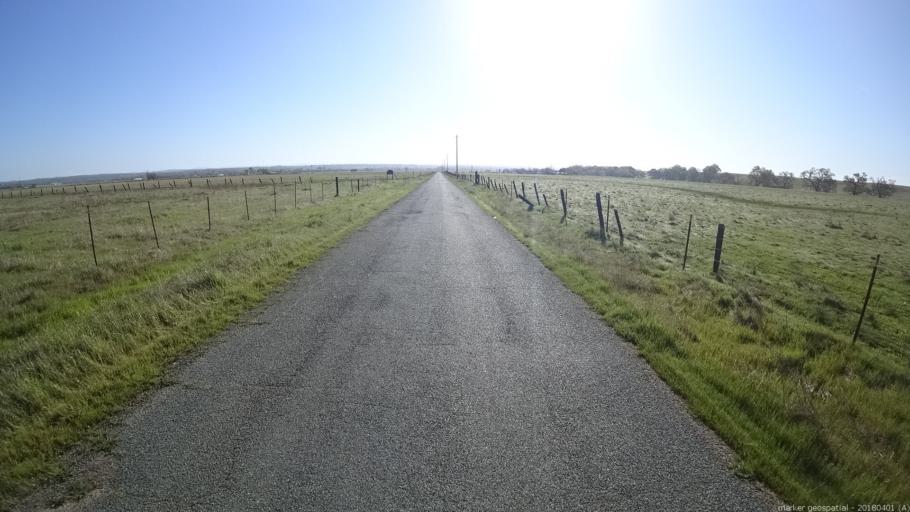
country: US
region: California
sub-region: Sacramento County
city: Rancho Murieta
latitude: 38.4203
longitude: -121.0348
